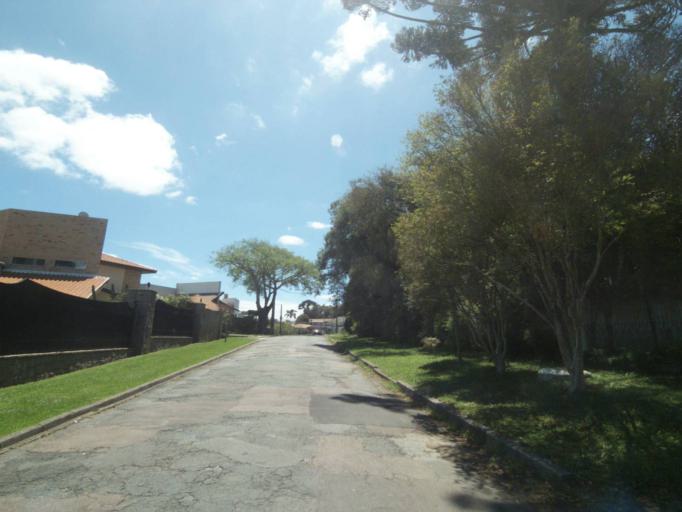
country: BR
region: Parana
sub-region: Curitiba
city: Curitiba
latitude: -25.3799
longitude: -49.2645
